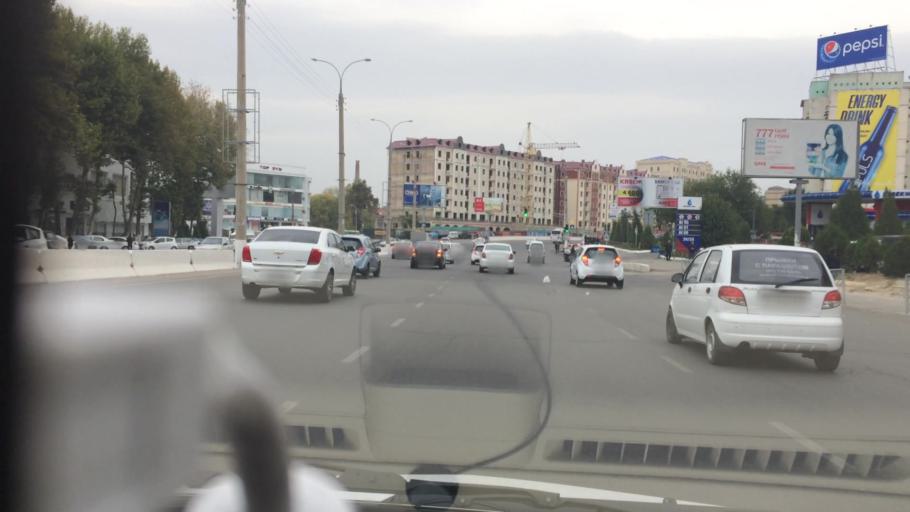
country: UZ
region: Toshkent
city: Salor
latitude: 41.3148
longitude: 69.3268
